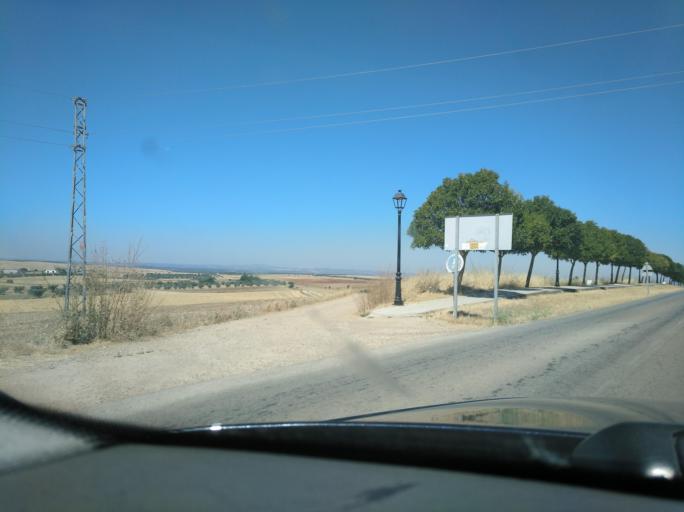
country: ES
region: Extremadura
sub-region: Provincia de Badajoz
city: Olivenza
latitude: 38.6866
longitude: -7.1072
